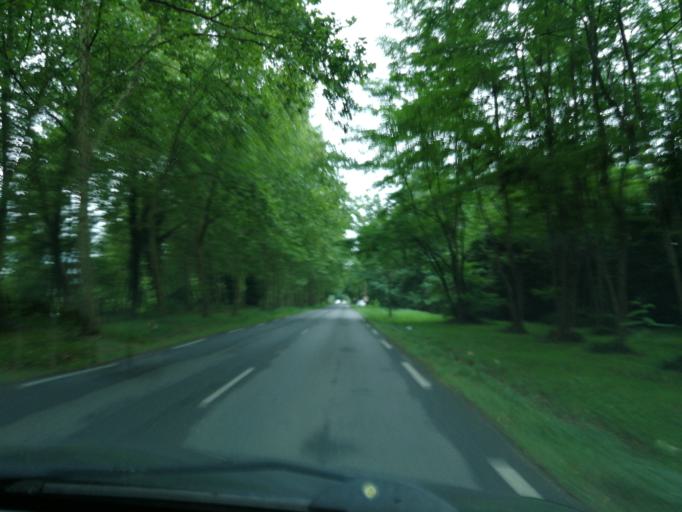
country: FR
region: Midi-Pyrenees
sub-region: Departement des Hautes-Pyrenees
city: Bazet
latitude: 43.2746
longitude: 0.0813
